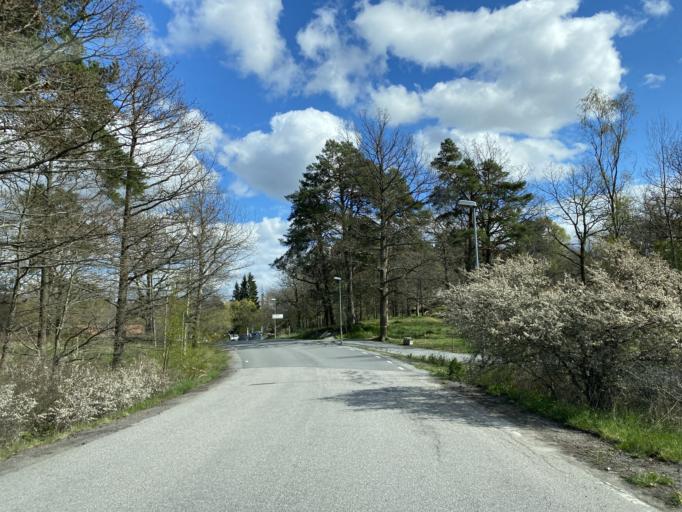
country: SE
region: Stockholm
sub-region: Stockholms Kommun
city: OEstermalm
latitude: 59.3648
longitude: 18.0694
